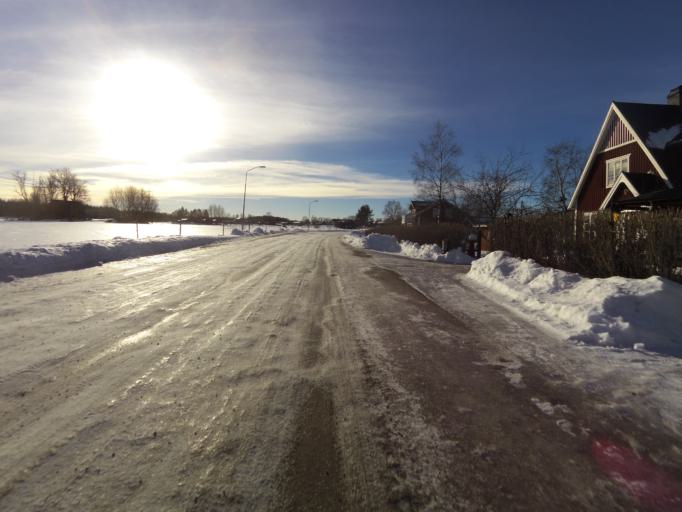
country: SE
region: Gaevleborg
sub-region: Gavle Kommun
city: Valbo
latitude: 60.6566
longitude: 17.0702
